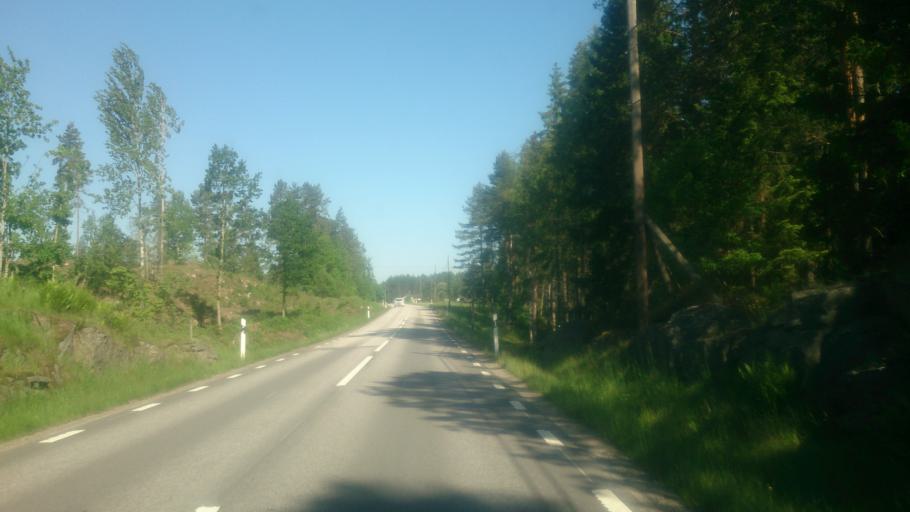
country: SE
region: OEstergoetland
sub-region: Atvidabergs Kommun
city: Atvidaberg
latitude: 58.1074
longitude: 16.1093
